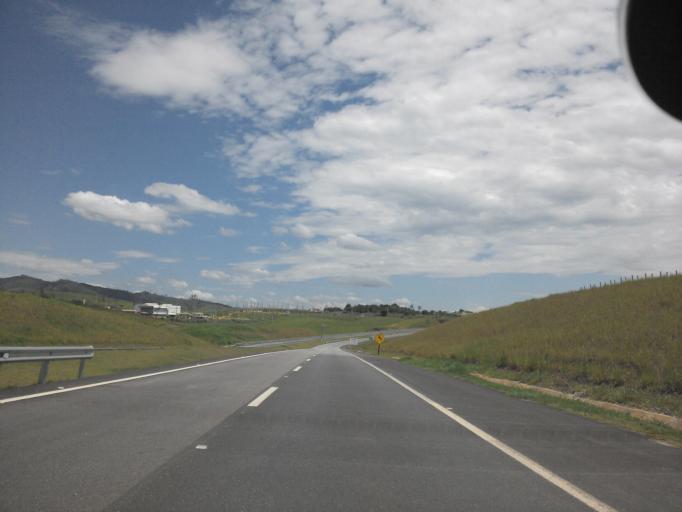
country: BR
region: Sao Paulo
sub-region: Taubate
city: Taubate
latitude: -23.0901
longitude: -45.5694
